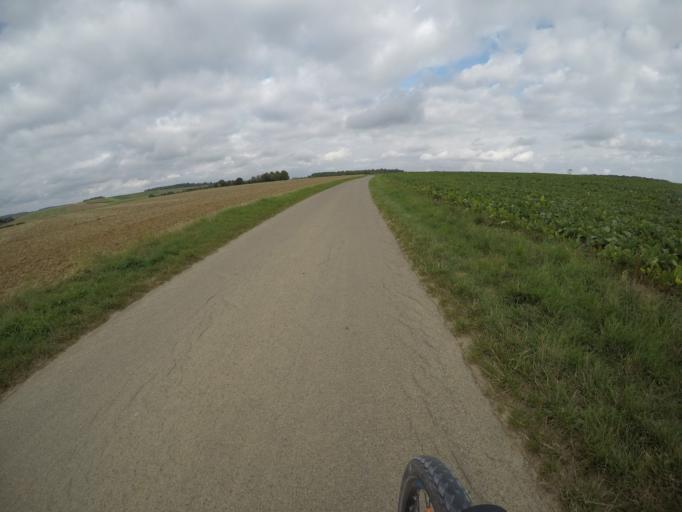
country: DE
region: Baden-Wuerttemberg
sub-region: Regierungsbezirk Stuttgart
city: Renningen
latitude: 48.7382
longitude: 8.9266
